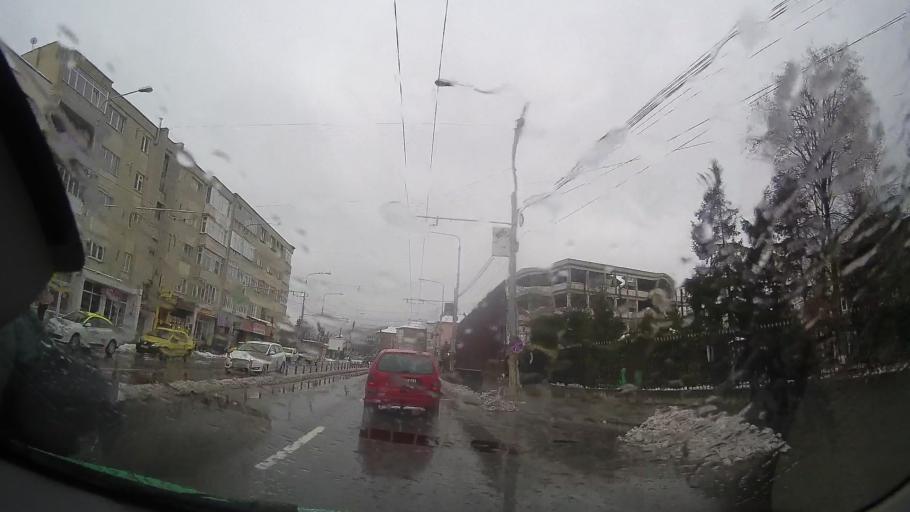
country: RO
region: Neamt
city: Piatra Neamt
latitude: 46.9337
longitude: 26.3592
